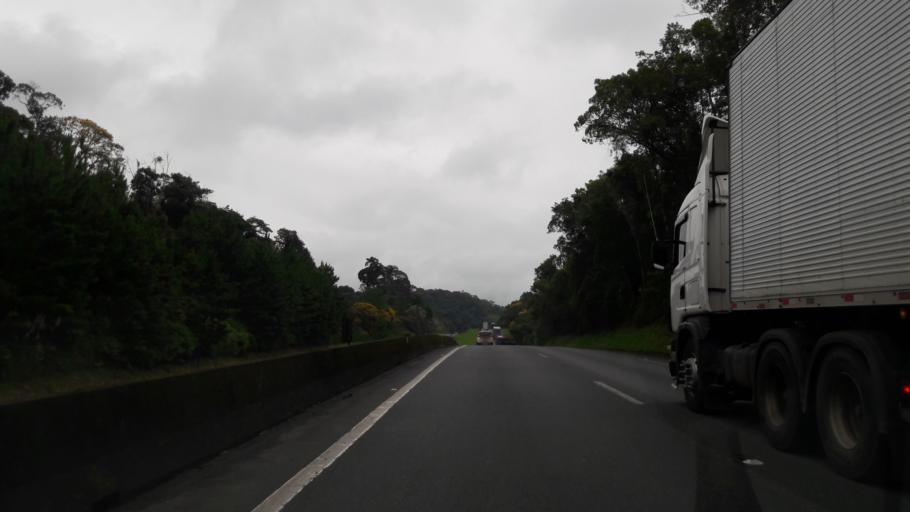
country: BR
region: Sao Paulo
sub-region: Cajati
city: Cajati
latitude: -24.9710
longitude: -48.3723
